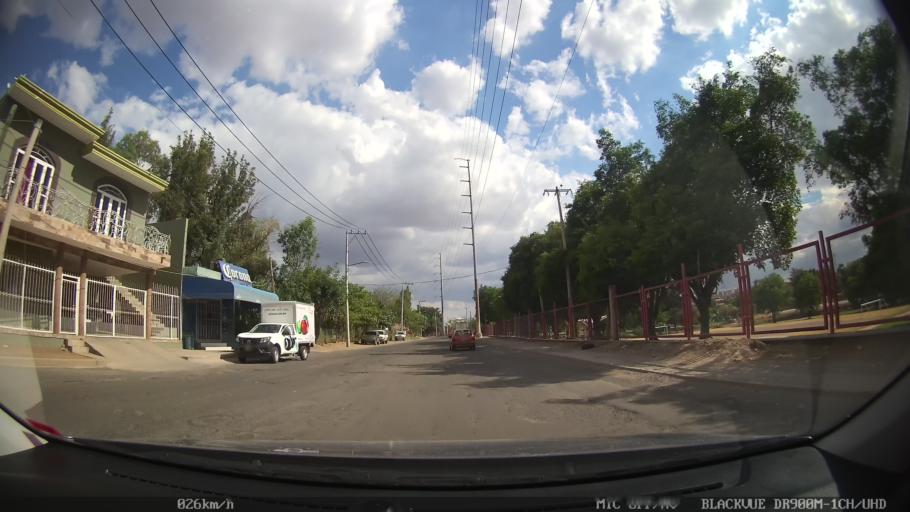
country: MX
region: Jalisco
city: Tlaquepaque
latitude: 20.6618
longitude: -103.2681
